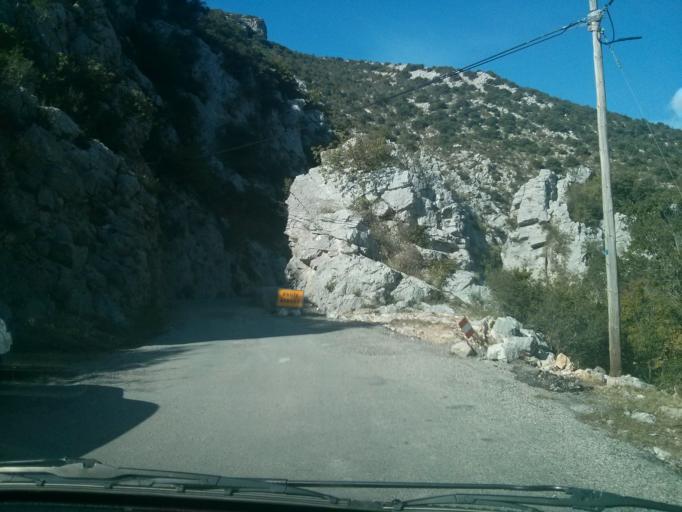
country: FR
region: Languedoc-Roussillon
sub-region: Departement du Gard
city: Saint-Hippolyte-du-Fort
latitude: 43.9606
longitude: 3.8070
